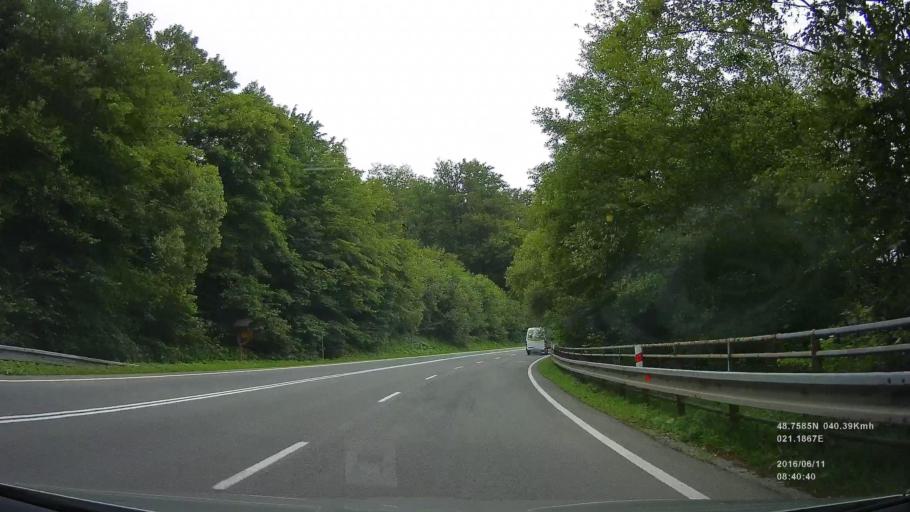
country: SK
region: Kosicky
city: Kosice
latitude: 48.7415
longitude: 21.2408
